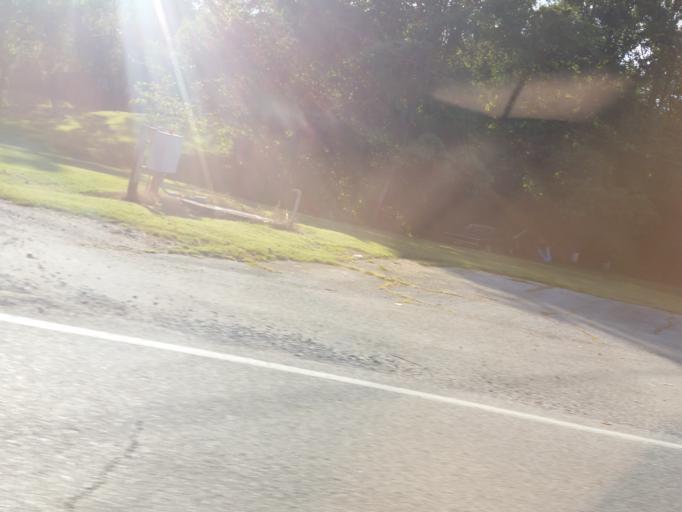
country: US
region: Tennessee
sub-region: Union County
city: Luttrell
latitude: 36.2252
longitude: -83.7454
